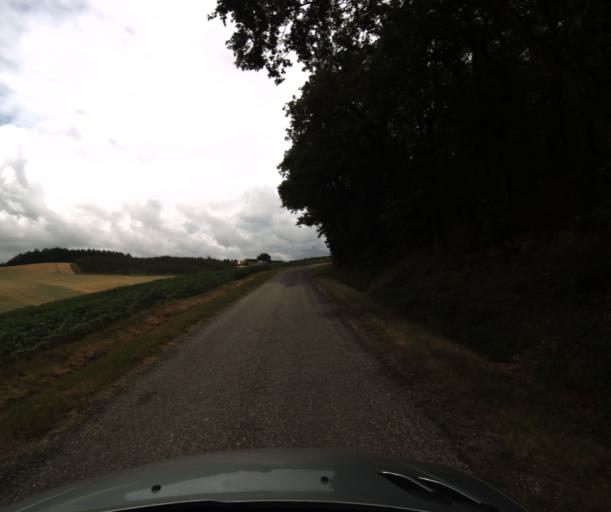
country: FR
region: Midi-Pyrenees
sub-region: Departement du Tarn-et-Garonne
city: Lavit
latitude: 43.9574
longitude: 0.8957
